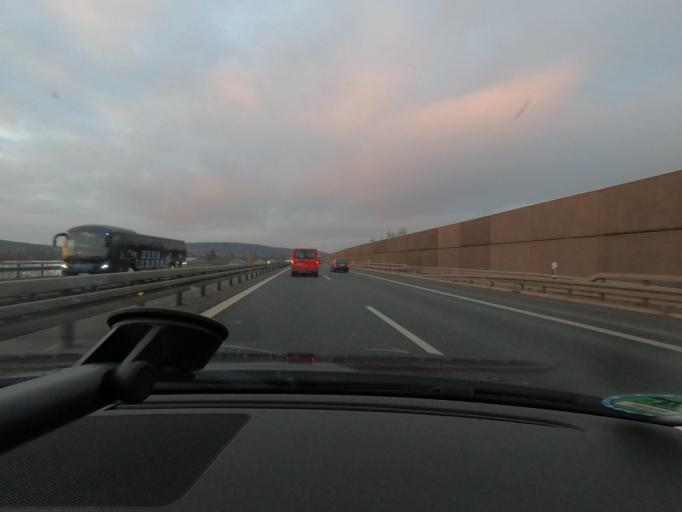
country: DE
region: Bavaria
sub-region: Upper Franconia
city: Forchheim
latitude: 49.7079
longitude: 11.0564
